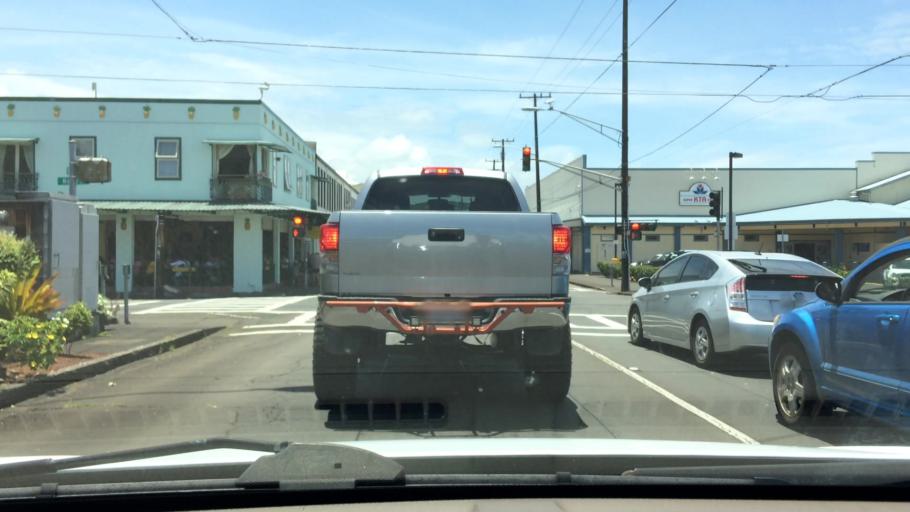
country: US
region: Hawaii
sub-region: Hawaii County
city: Hilo
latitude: 19.7225
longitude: -155.0858
